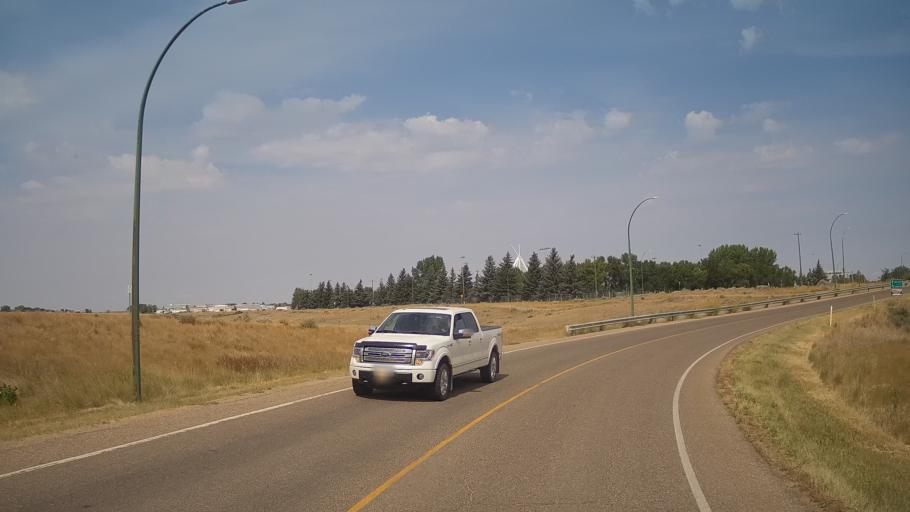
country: CA
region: Alberta
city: Medicine Hat
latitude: 50.0109
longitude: -110.6848
